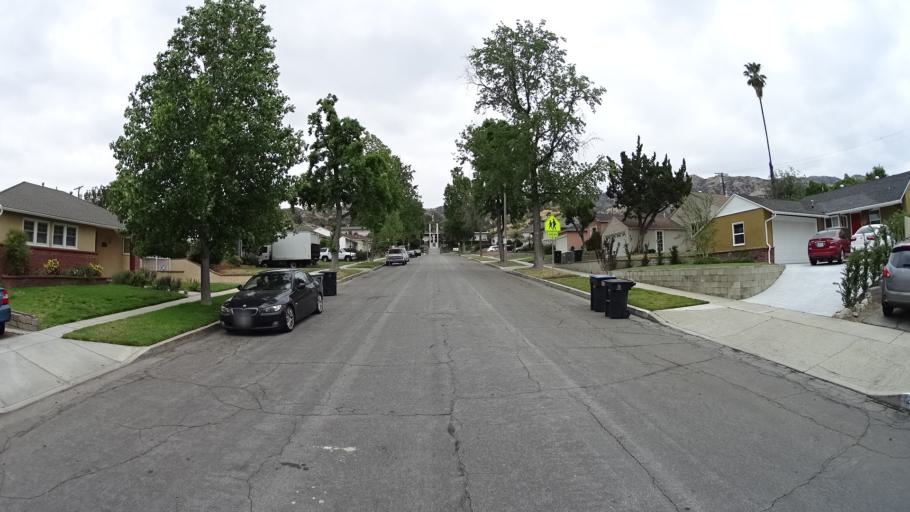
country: US
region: California
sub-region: Los Angeles County
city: Burbank
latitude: 34.2089
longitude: -118.3364
